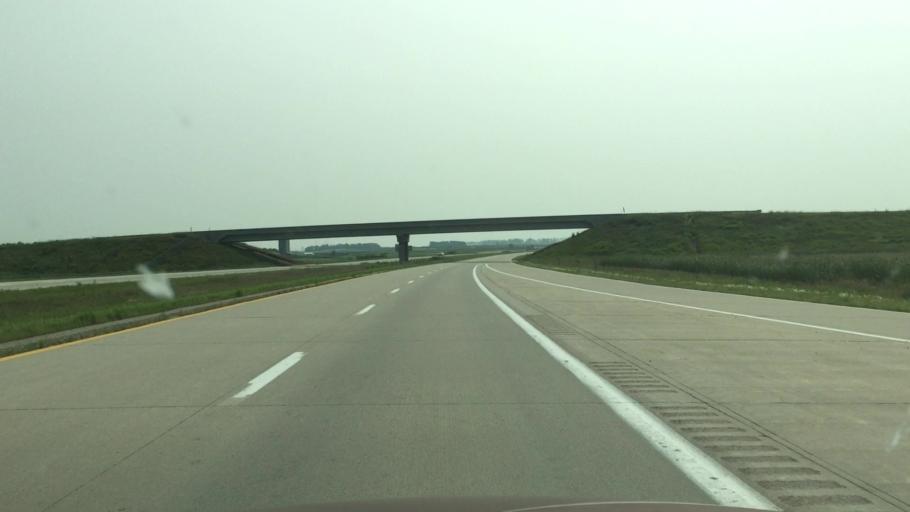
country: US
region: Iowa
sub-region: Osceola County
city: Sibley
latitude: 43.3839
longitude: -95.7440
